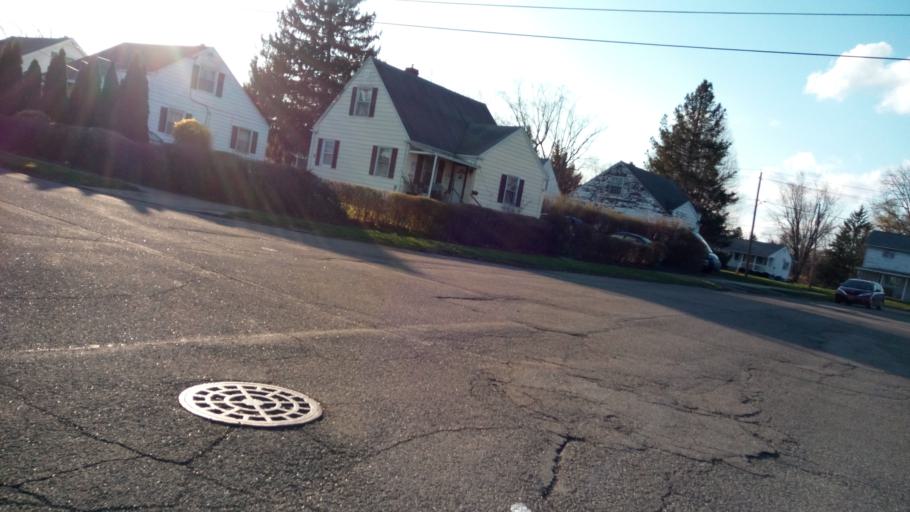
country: US
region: New York
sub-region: Chemung County
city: Elmira
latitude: 42.0806
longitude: -76.7830
